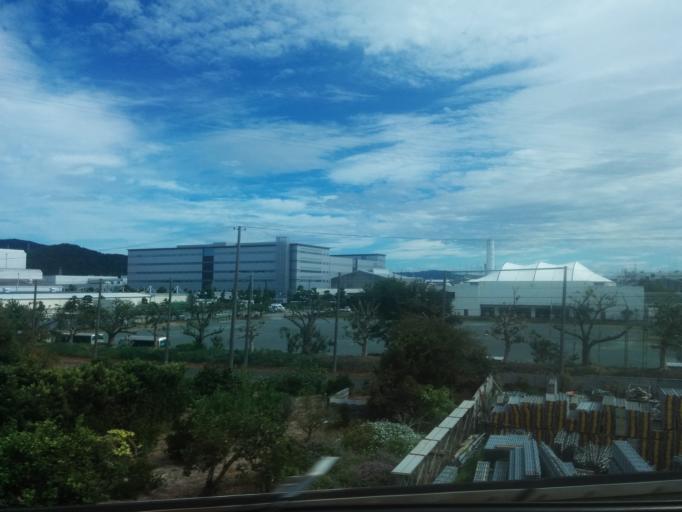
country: JP
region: Shizuoka
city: Kosai-shi
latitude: 34.7157
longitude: 137.4804
